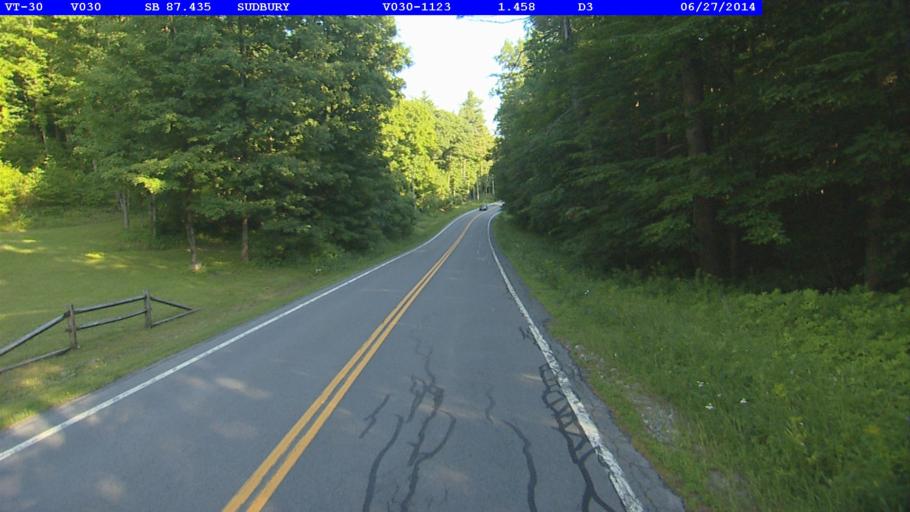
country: US
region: Vermont
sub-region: Rutland County
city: Brandon
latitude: 43.7699
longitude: -73.1988
